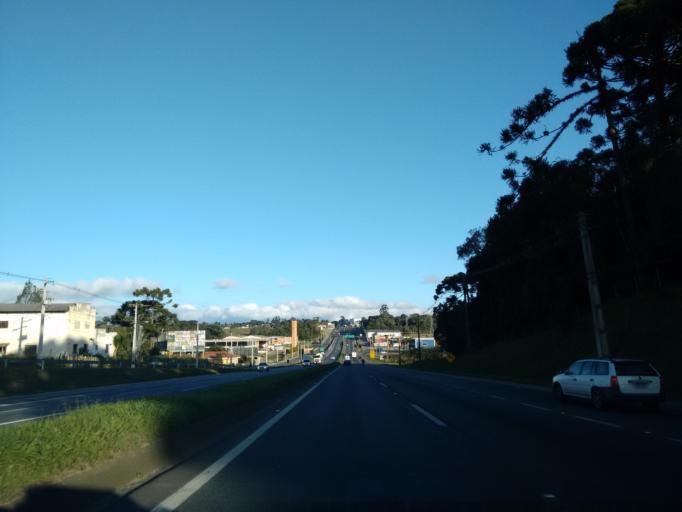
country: BR
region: Parana
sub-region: Sao Jose Dos Pinhais
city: Sao Jose dos Pinhais
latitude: -25.5725
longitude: -49.1806
